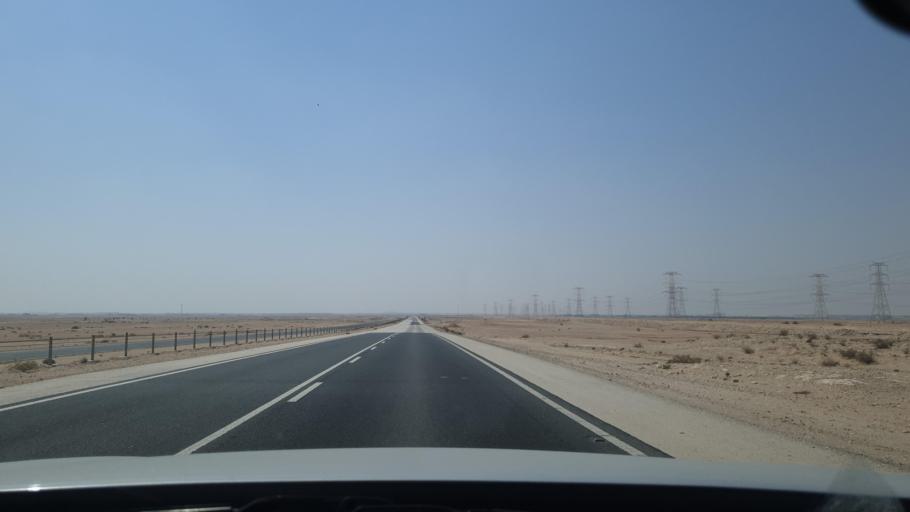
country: QA
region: Al Khawr
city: Al Khawr
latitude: 25.7193
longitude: 51.4512
